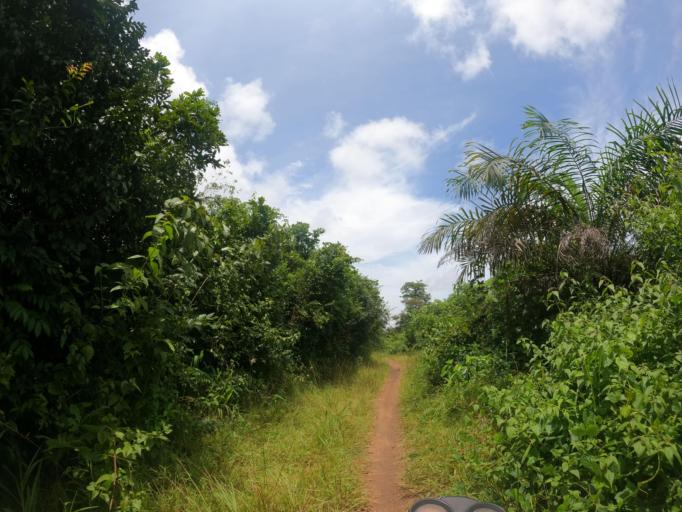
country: SL
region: Northern Province
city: Binkolo
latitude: 9.1468
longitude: -12.2451
